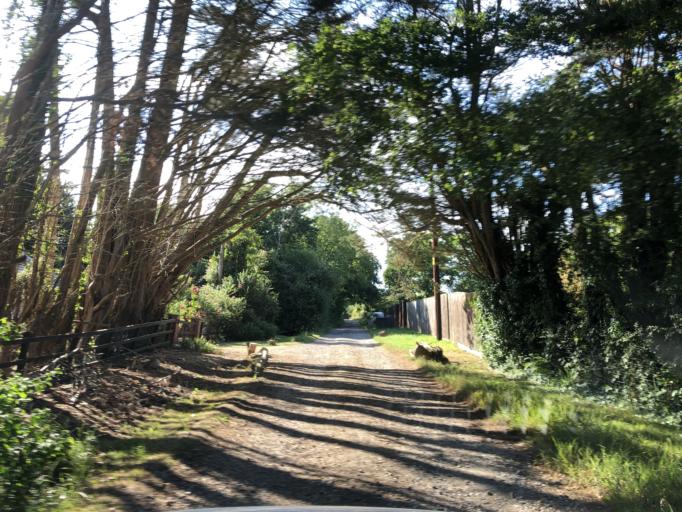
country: GB
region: England
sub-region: Isle of Wight
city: Shalfleet
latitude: 50.7091
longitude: -1.4390
